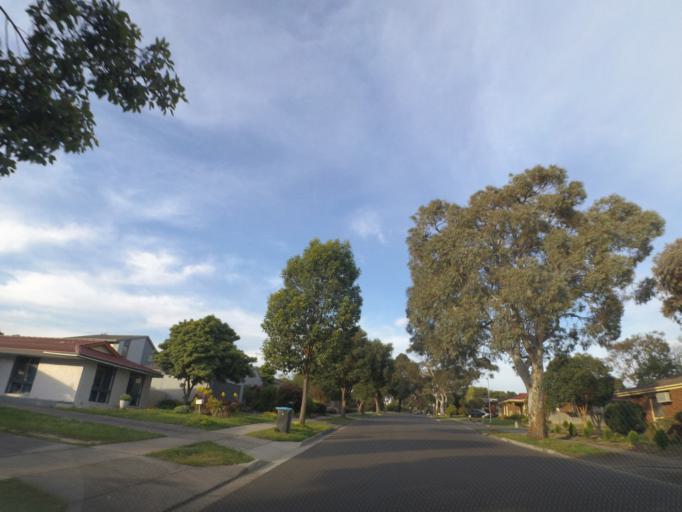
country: AU
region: Victoria
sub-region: Knox
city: Wantirna
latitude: -37.8561
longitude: 145.2336
